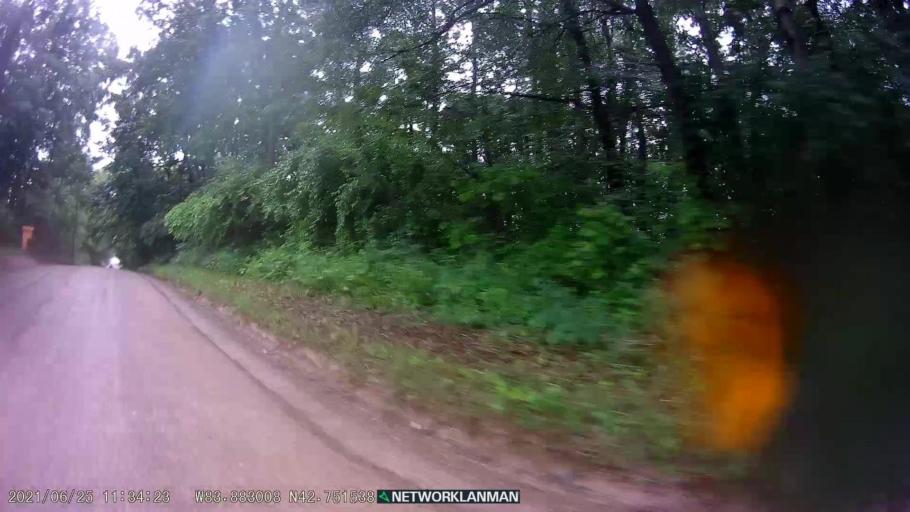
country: US
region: Michigan
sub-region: Genesee County
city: Argentine
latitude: 42.7514
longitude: -83.8828
